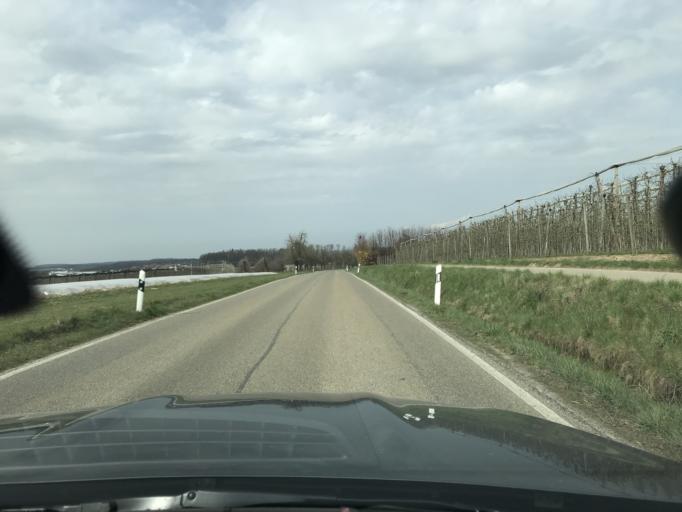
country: DE
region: Baden-Wuerttemberg
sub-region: Regierungsbezirk Stuttgart
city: Burgstetten
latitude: 48.9084
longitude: 9.3796
